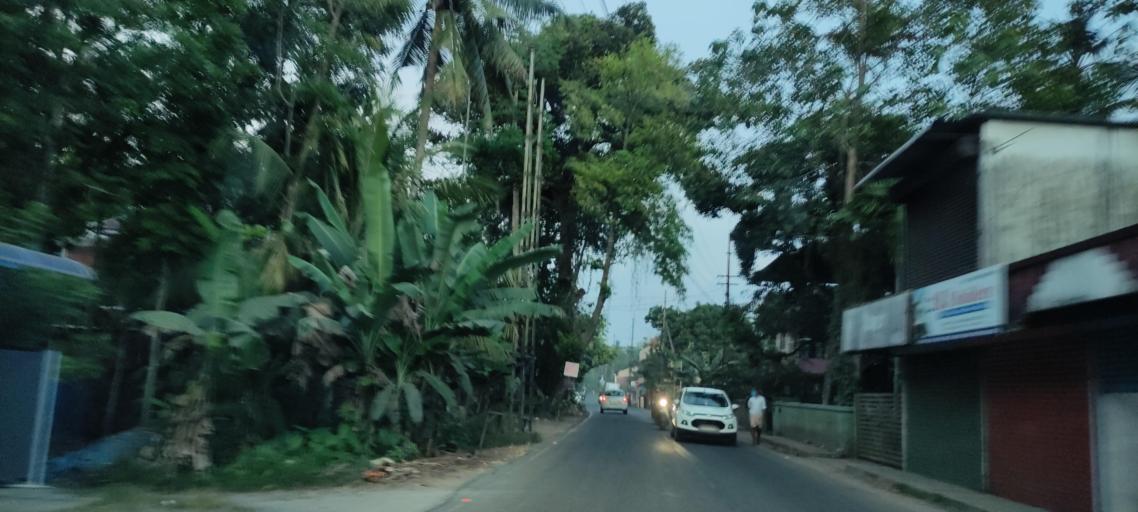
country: IN
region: Kerala
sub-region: Alappuzha
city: Kutiatodu
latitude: 9.7685
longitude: 76.3206
